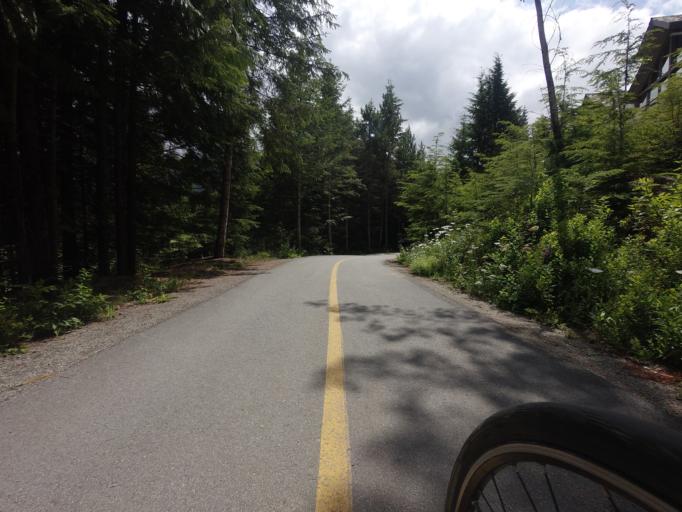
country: CA
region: British Columbia
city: Whistler
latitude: 50.1130
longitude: -122.9671
